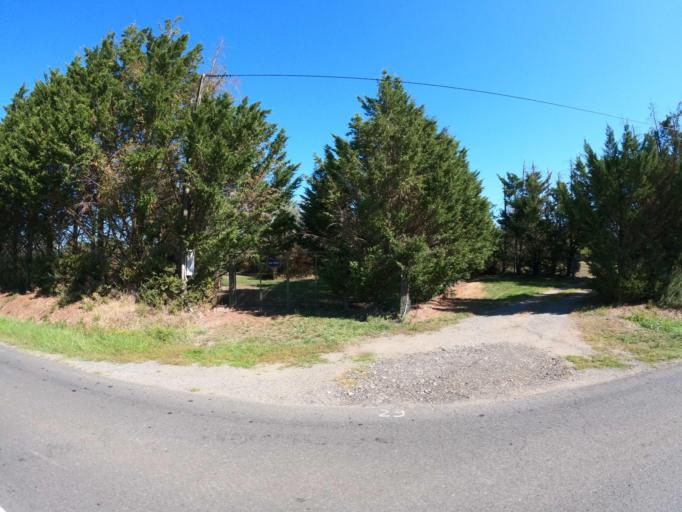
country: FR
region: Poitou-Charentes
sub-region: Departement de la Vienne
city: Saulge
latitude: 46.3763
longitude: 0.9263
